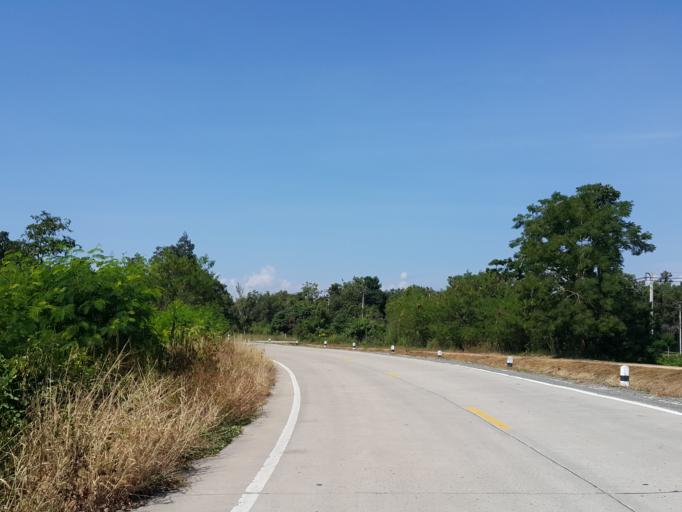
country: TH
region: Chiang Mai
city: San Sai
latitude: 18.8781
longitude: 99.1641
